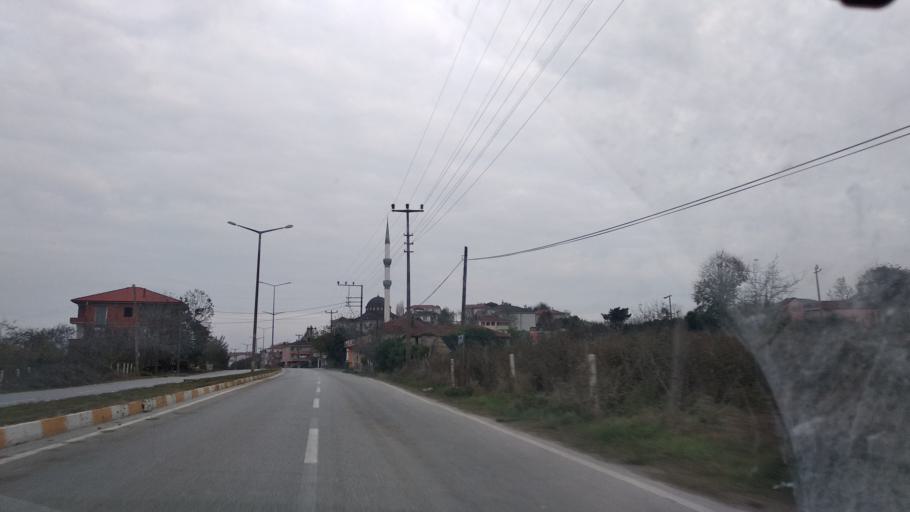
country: TR
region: Sakarya
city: Karasu
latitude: 41.0986
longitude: 30.6727
